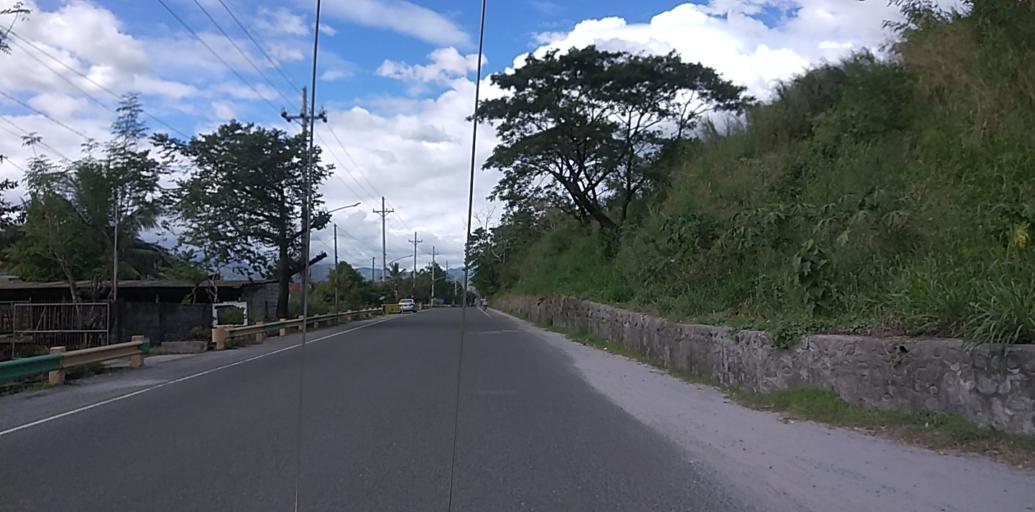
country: PH
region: Central Luzon
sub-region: Province of Pampanga
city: Dolores
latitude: 15.0923
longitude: 120.5341
